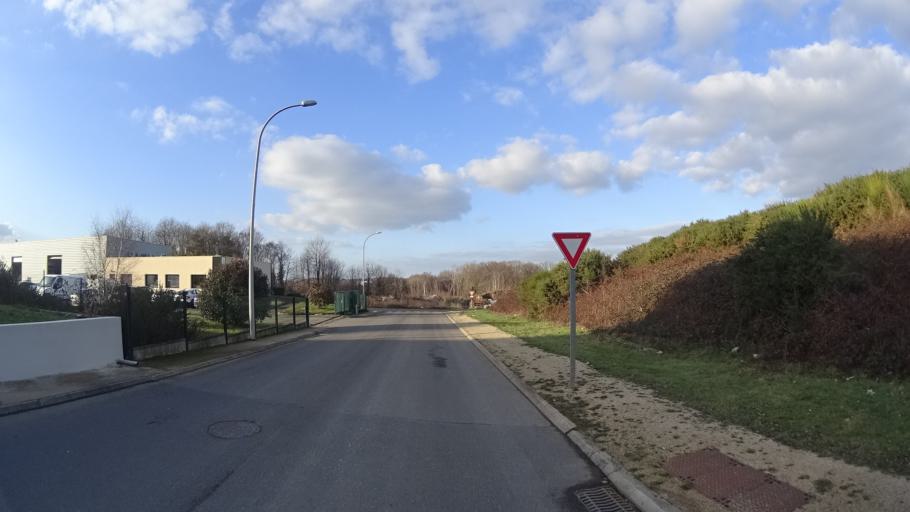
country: FR
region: Pays de la Loire
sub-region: Departement de la Loire-Atlantique
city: Saint-Nicolas-de-Redon
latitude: 47.6301
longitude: -2.0538
